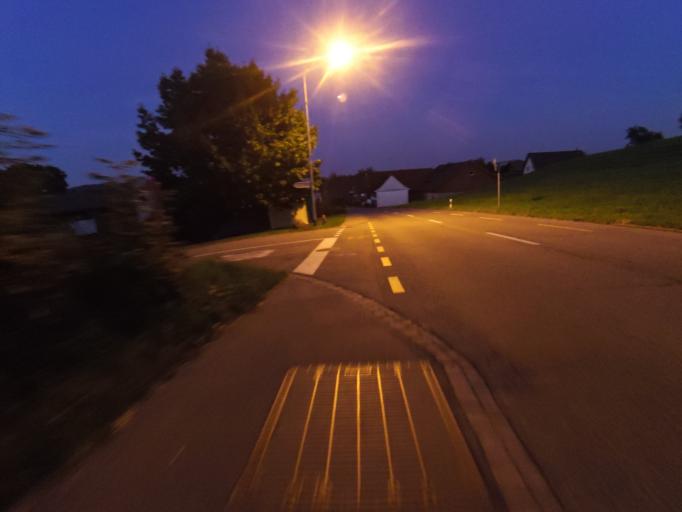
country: CH
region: Thurgau
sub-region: Weinfelden District
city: Maerstetten-Dorf
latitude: 47.5676
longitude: 9.0523
